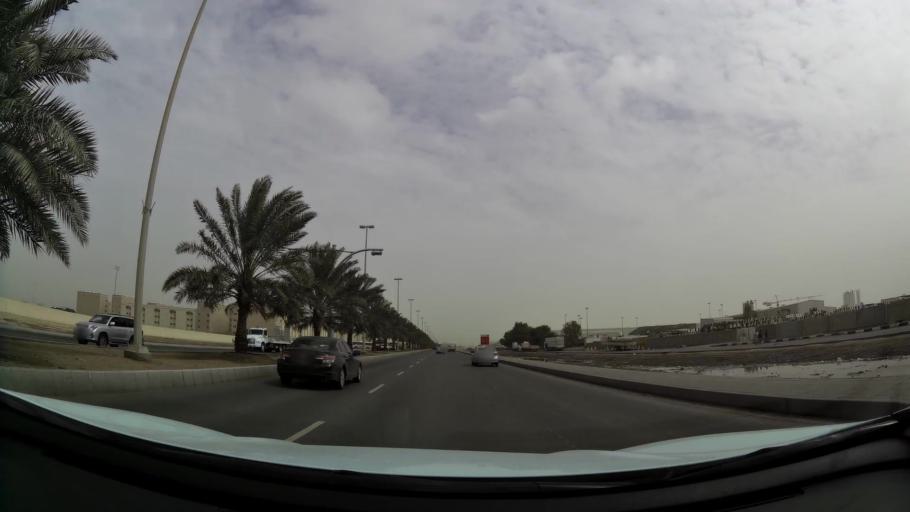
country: AE
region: Abu Dhabi
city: Abu Dhabi
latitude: 24.3459
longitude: 54.5070
